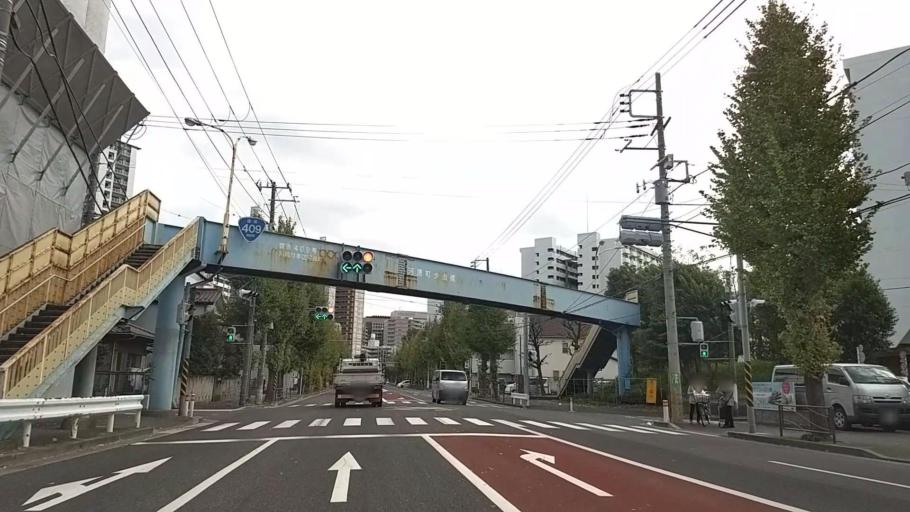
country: JP
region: Kanagawa
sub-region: Kawasaki-shi
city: Kawasaki
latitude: 35.5422
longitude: 139.6947
